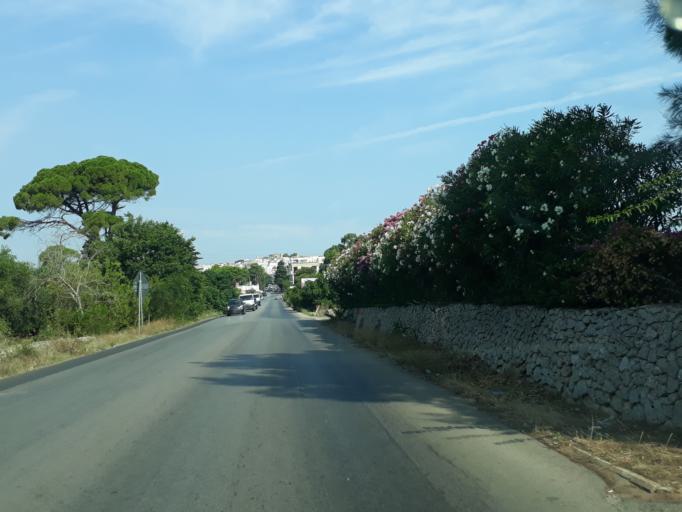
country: IT
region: Apulia
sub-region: Provincia di Brindisi
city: Carovigno
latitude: 40.6965
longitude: 17.6678
